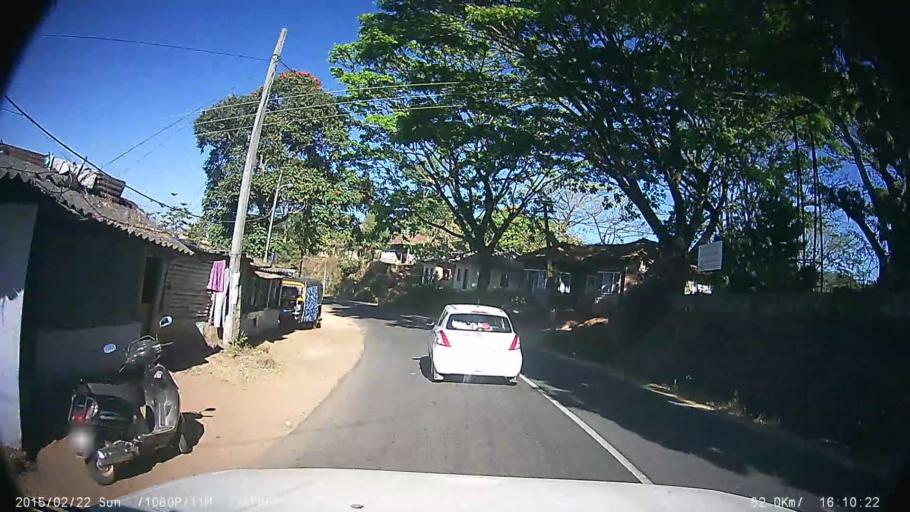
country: IN
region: Tamil Nadu
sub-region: Theni
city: Gudalur
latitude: 9.5694
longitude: 77.0862
